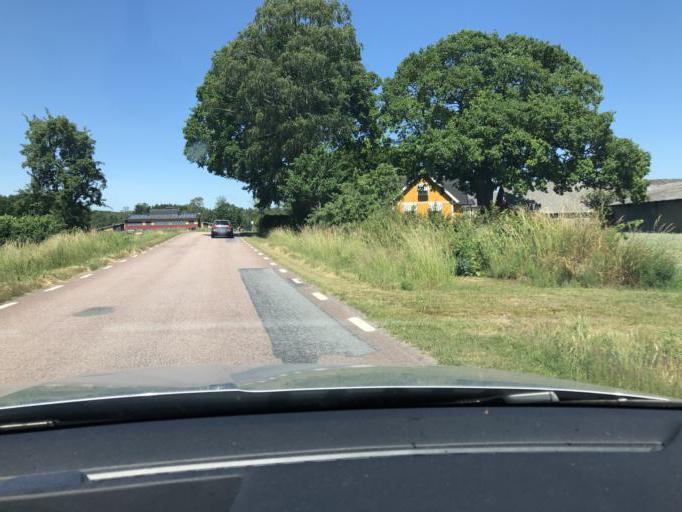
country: SE
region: Blekinge
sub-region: Olofstroms Kommun
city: Jamshog
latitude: 56.1807
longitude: 14.6121
